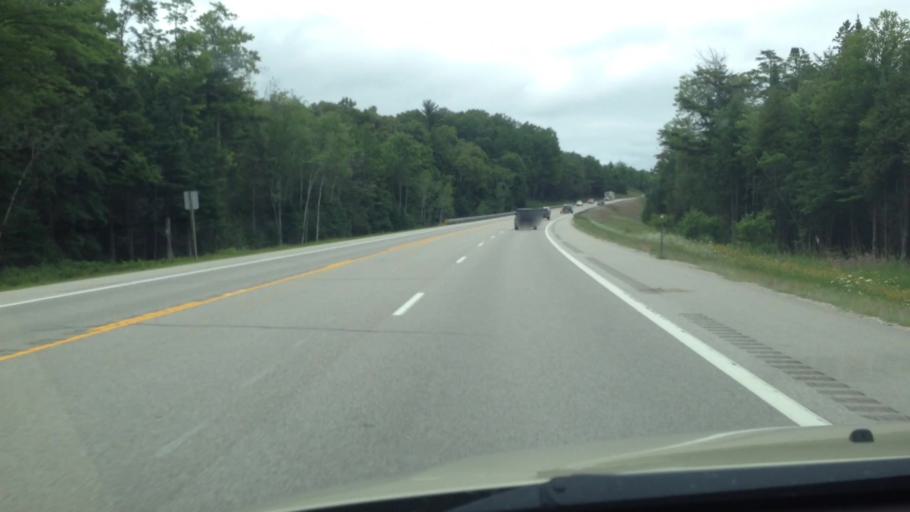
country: US
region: Michigan
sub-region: Luce County
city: Newberry
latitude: 46.0701
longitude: -85.2070
